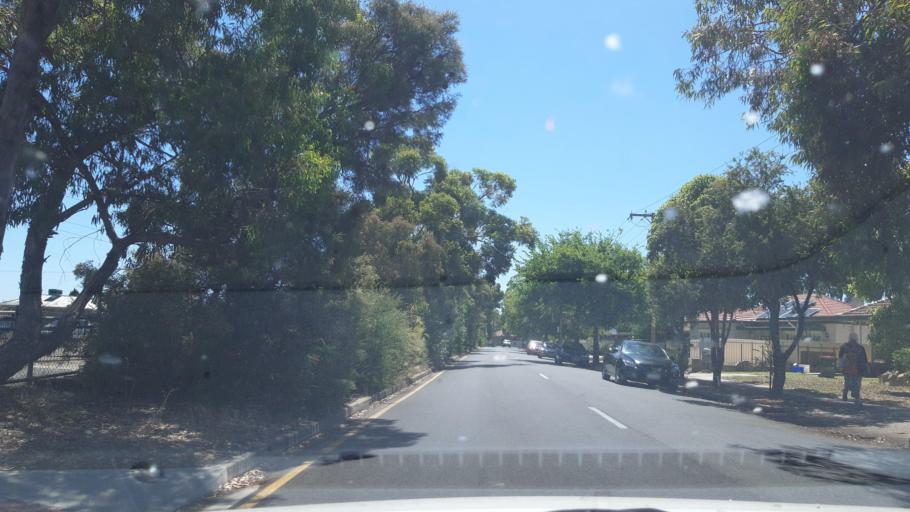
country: AU
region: South Australia
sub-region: Marion
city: South Plympton
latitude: -34.9823
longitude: 138.5677
